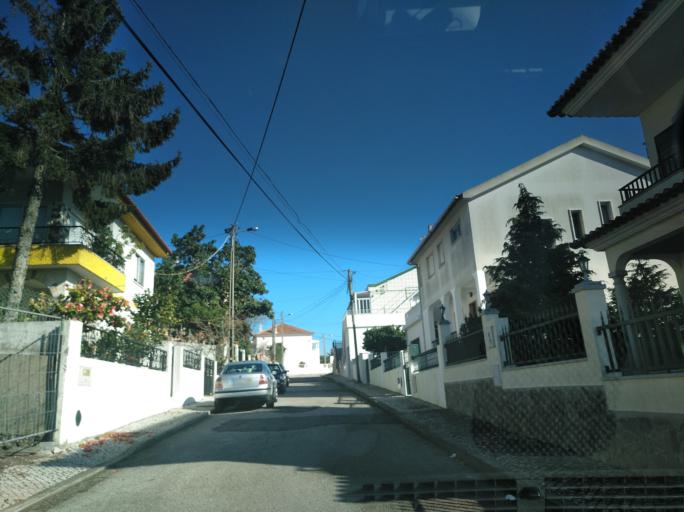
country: PT
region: Lisbon
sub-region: Odivelas
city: Famoes
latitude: 38.7991
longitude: -9.2178
